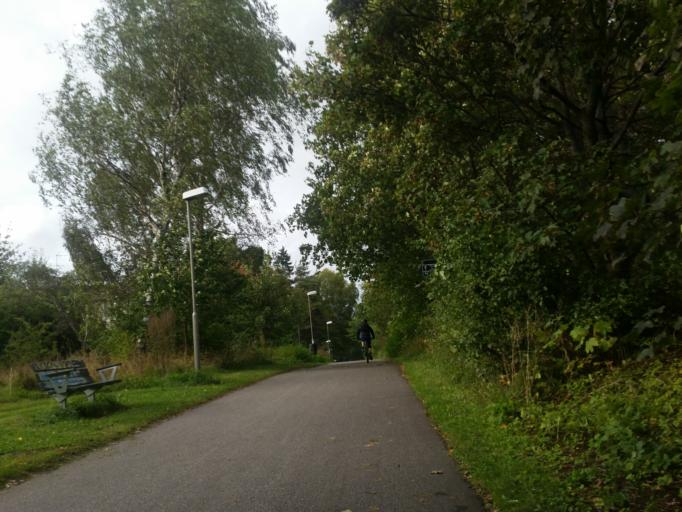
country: SE
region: Stockholm
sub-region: Stockholms Kommun
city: Arsta
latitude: 59.2638
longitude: 18.0979
